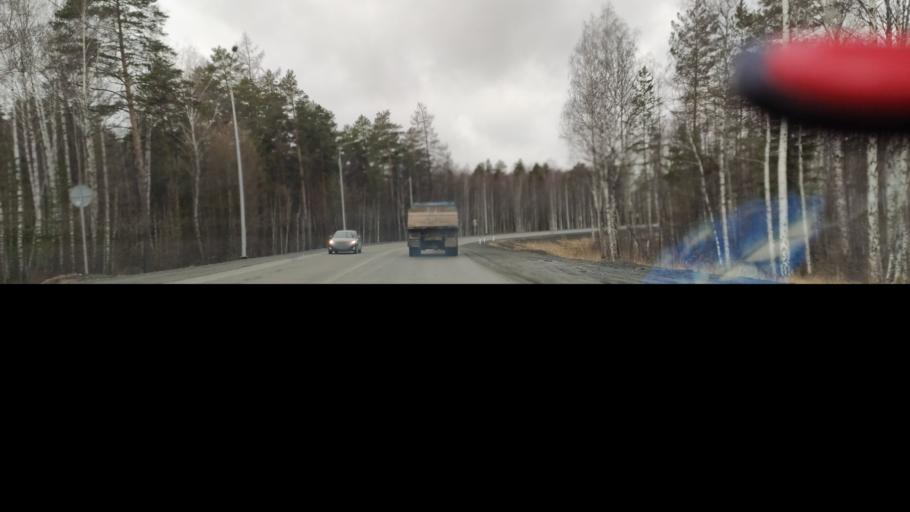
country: RU
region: Sverdlovsk
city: Talitsa
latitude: 56.8504
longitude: 60.0597
